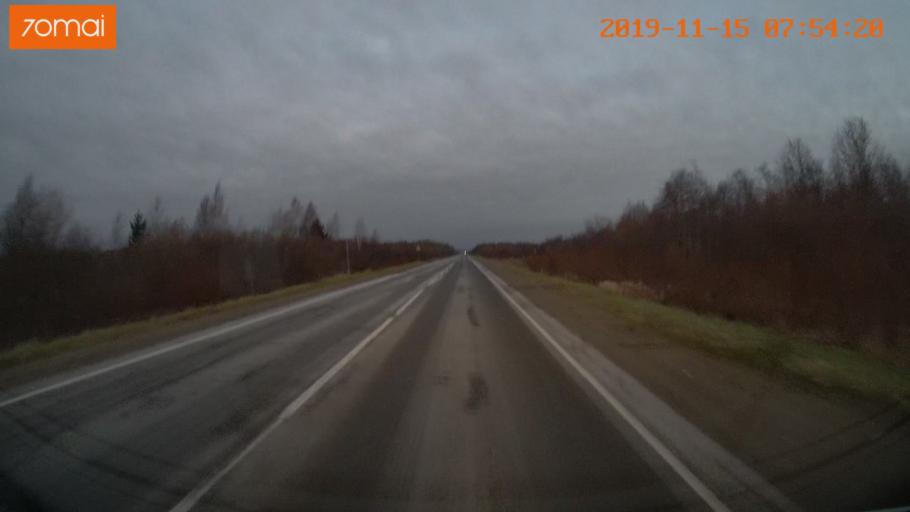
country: RU
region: Vologda
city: Cherepovets
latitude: 58.8976
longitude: 38.1771
